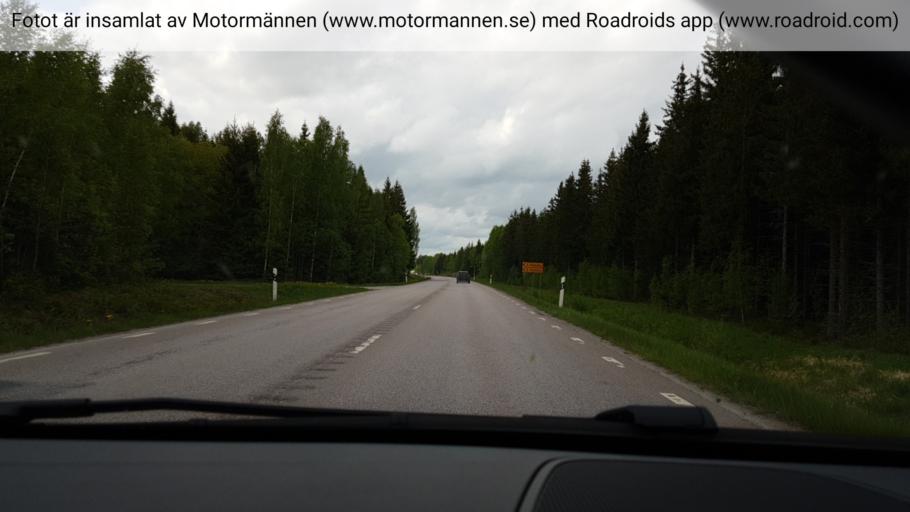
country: SE
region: Uppsala
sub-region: Tierps Kommun
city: Orbyhus
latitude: 60.2712
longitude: 17.6051
